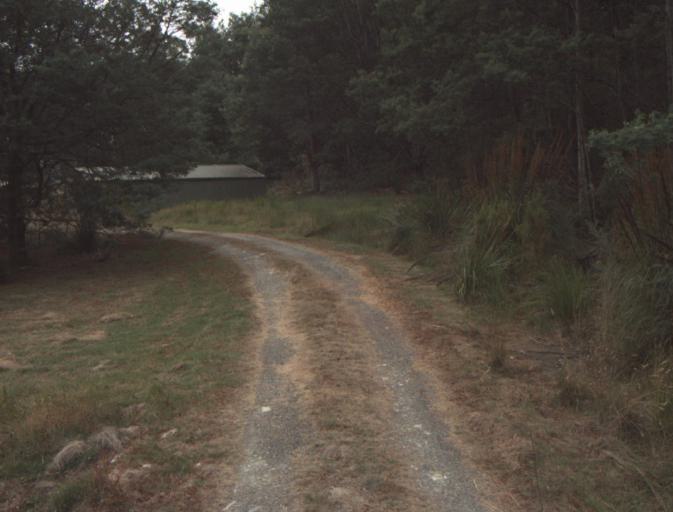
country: AU
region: Tasmania
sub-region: Launceston
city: Mayfield
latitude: -41.2685
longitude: 147.1650
